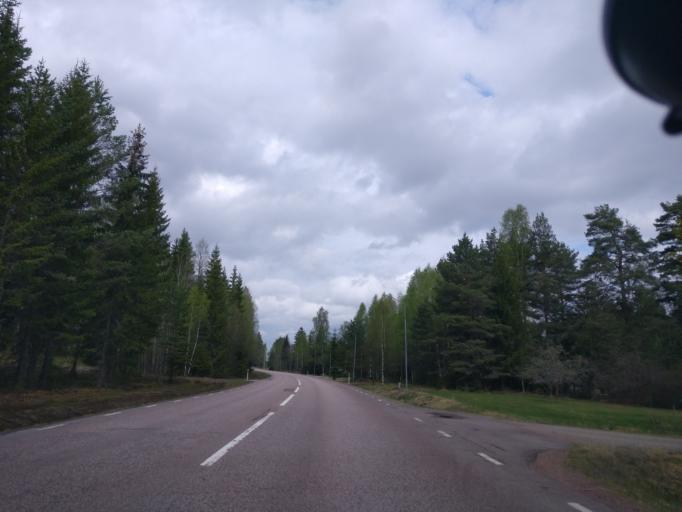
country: SE
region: Vaermland
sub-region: Hagfors Kommun
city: Ekshaerad
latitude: 60.1423
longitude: 13.5250
